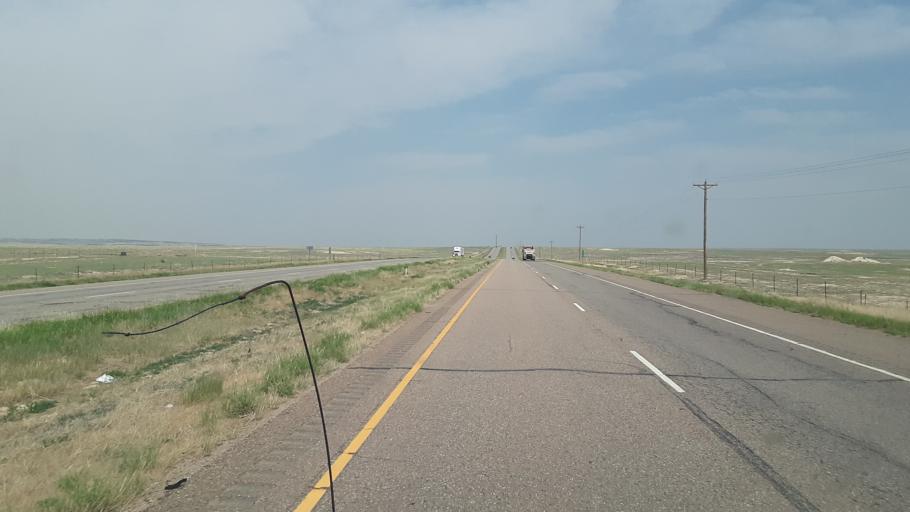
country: US
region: Colorado
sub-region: Fremont County
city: Penrose
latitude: 38.3669
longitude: -104.9111
